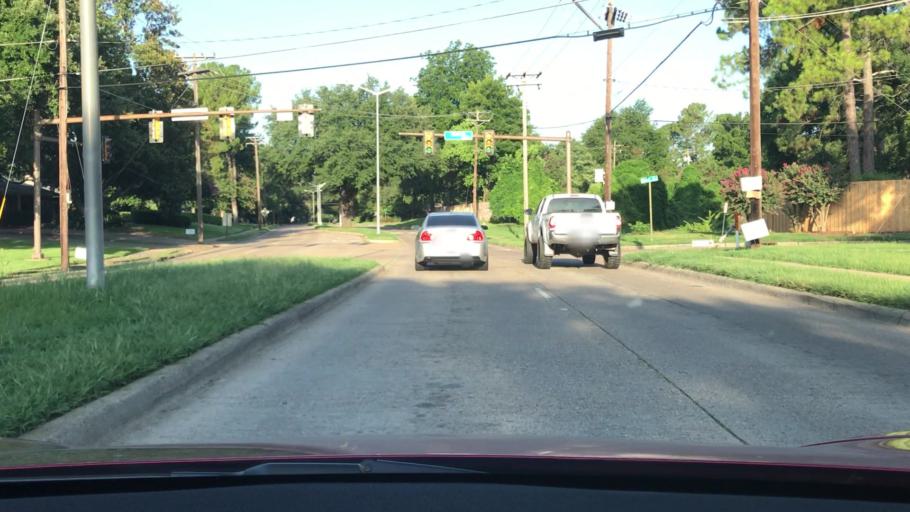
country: US
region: Louisiana
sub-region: Bossier Parish
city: Bossier City
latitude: 32.4565
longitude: -93.7283
